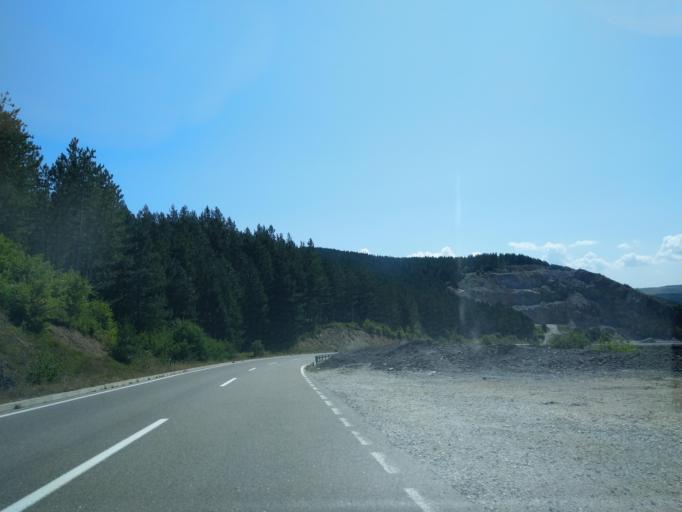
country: RS
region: Central Serbia
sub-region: Zlatiborski Okrug
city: Sjenica
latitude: 43.3010
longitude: 19.9332
